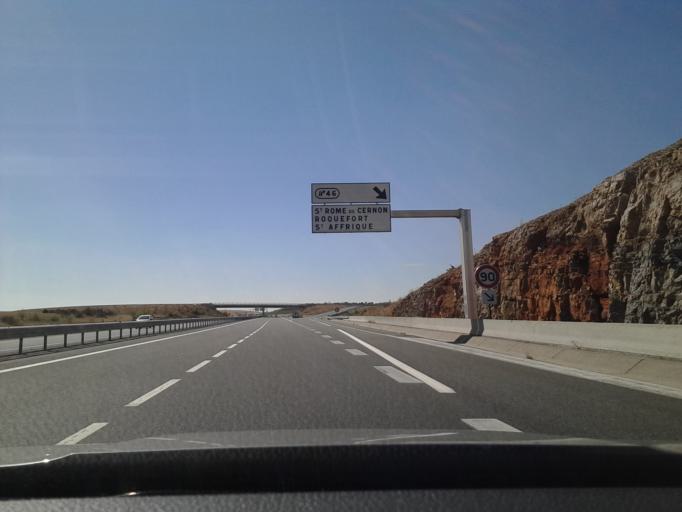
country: FR
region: Midi-Pyrenees
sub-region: Departement de l'Aveyron
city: Creissels
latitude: 44.0361
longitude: 3.0621
